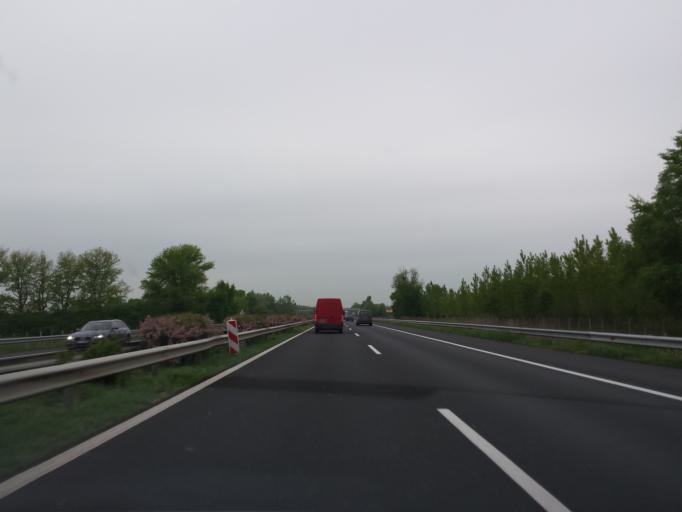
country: HU
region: Gyor-Moson-Sopron
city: Kimle
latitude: 47.7855
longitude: 17.3388
